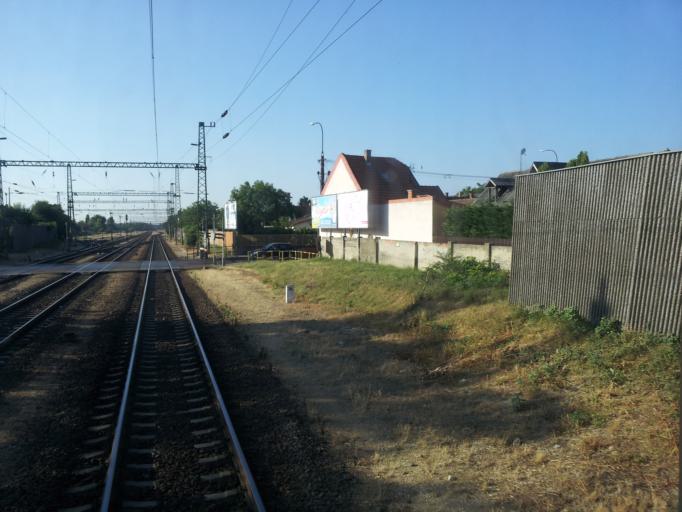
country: HU
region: Budapest
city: Budapest XXIII. keruelet
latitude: 47.4085
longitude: 19.1187
